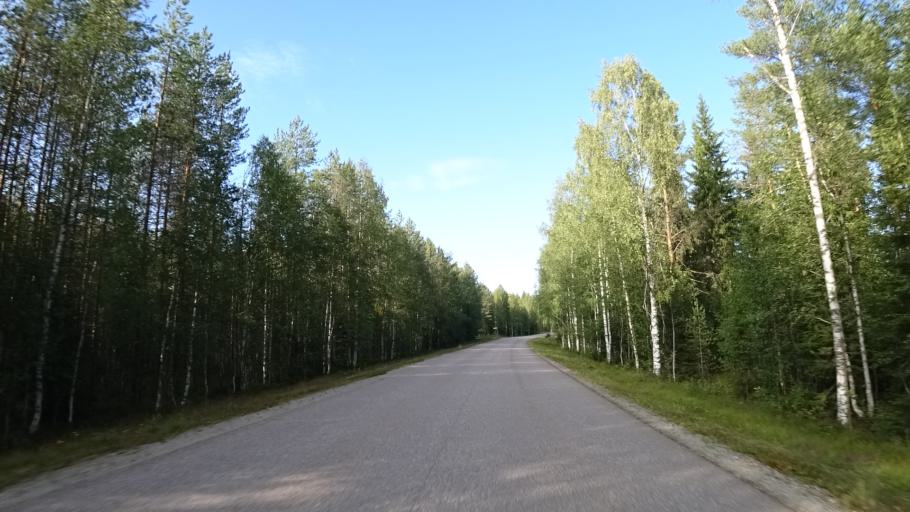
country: FI
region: North Karelia
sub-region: Joensuu
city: Eno
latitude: 63.0246
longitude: 30.5015
